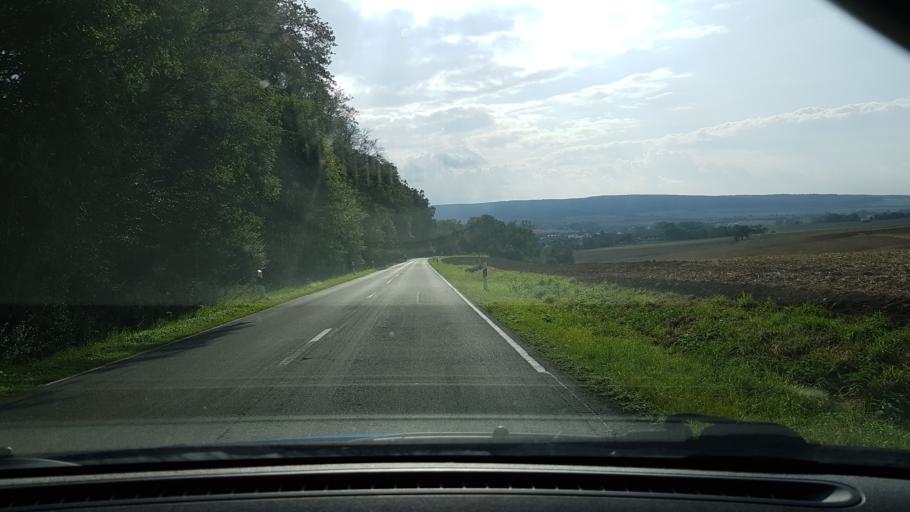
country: DE
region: Lower Saxony
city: Messenkamp
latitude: 52.2429
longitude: 9.4331
